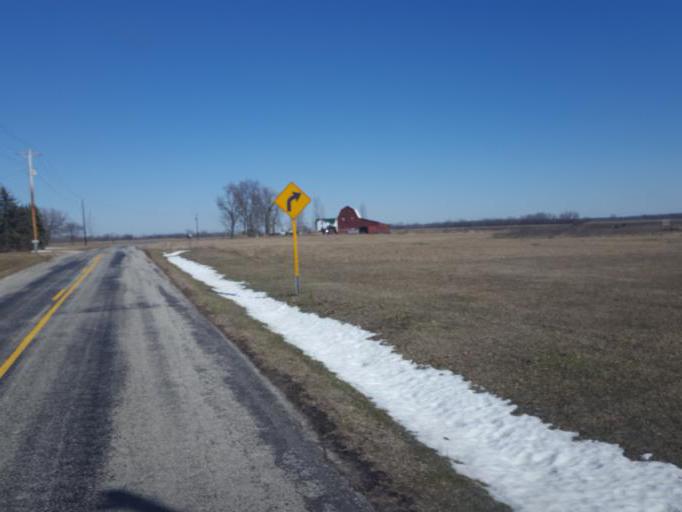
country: US
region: Ohio
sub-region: Wyandot County
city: Upper Sandusky
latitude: 40.6807
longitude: -83.2987
